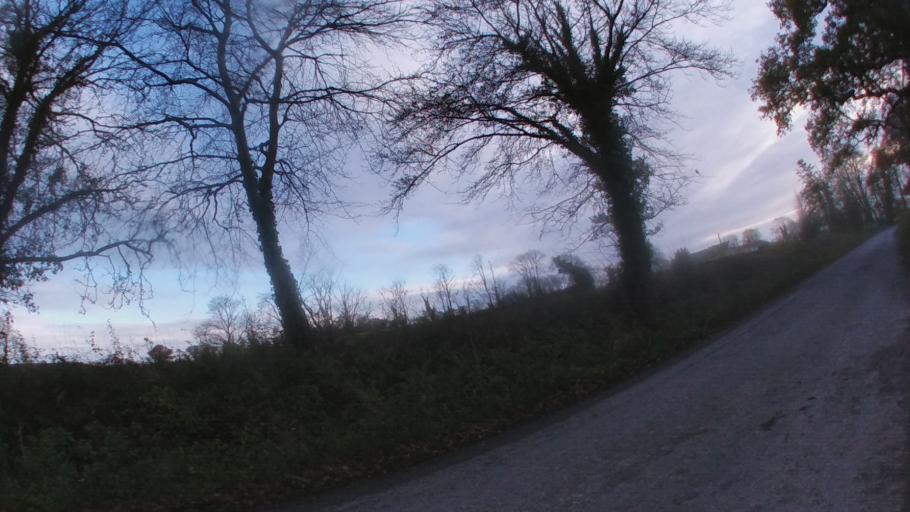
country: IE
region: Leinster
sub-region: Kilkenny
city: Kilkenny
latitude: 52.6904
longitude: -7.1729
